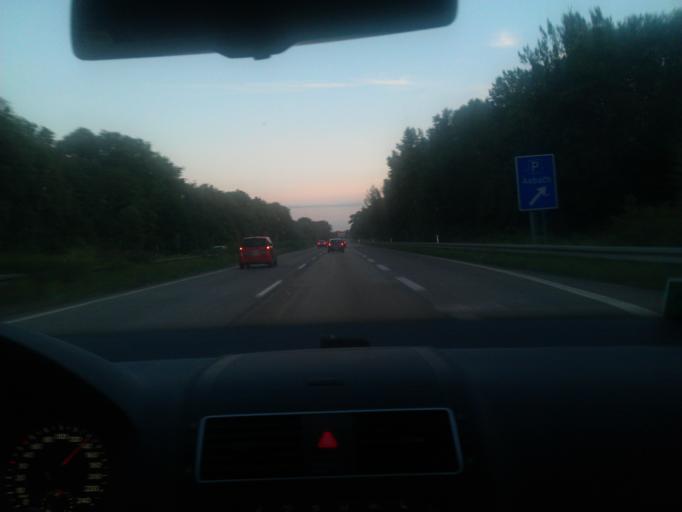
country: DE
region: North Rhine-Westphalia
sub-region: Regierungsbezirk Munster
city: Ladbergen
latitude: 52.1408
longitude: 7.7274
